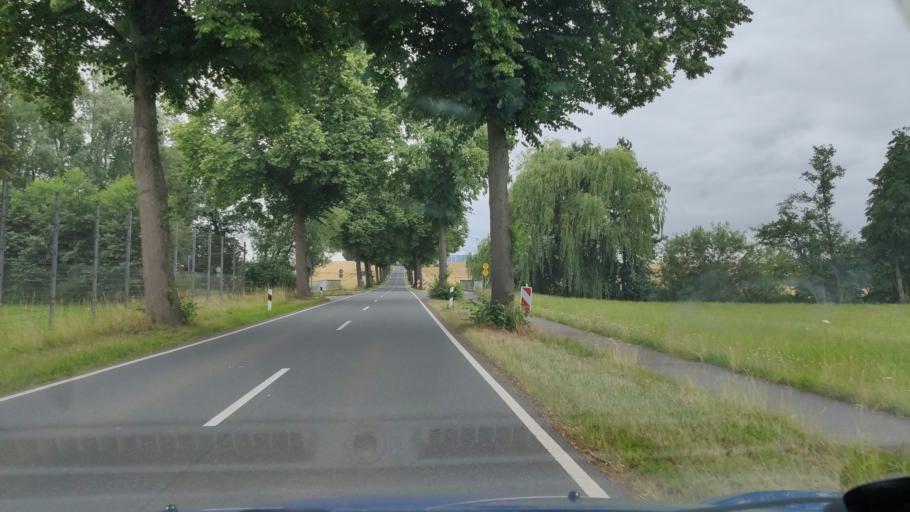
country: DE
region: Lower Saxony
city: Bad Munder am Deister
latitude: 52.1606
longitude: 9.4852
